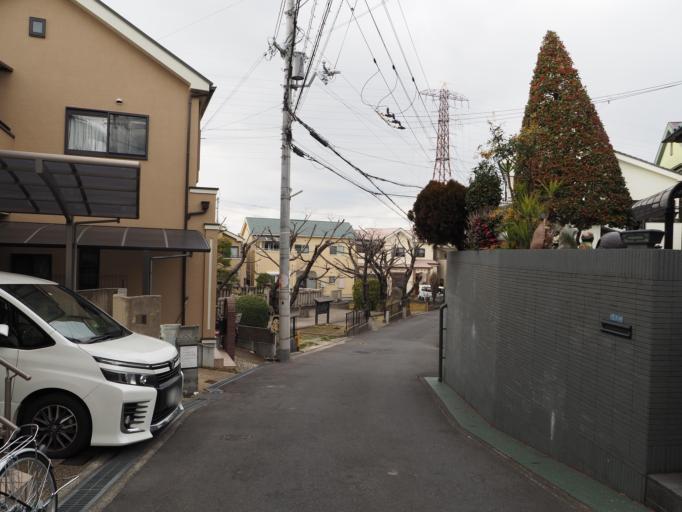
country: JP
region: Osaka
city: Hirakata
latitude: 34.7817
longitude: 135.6708
